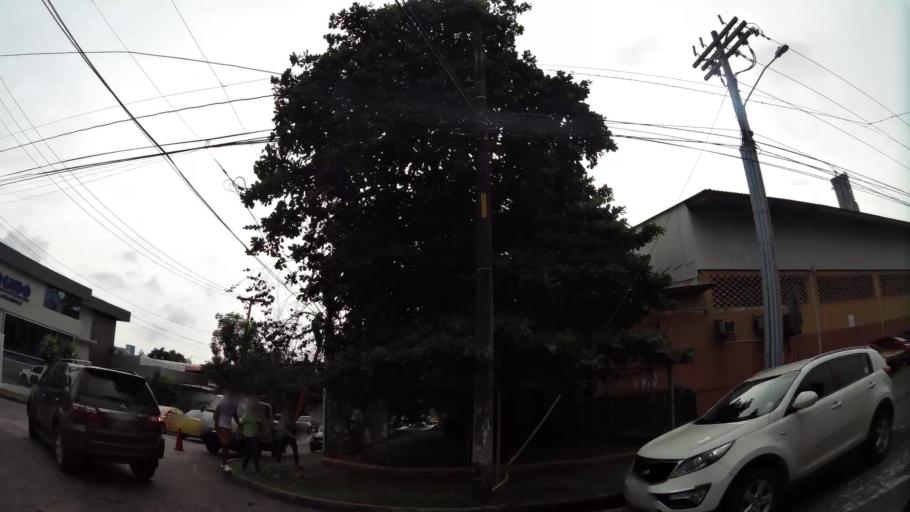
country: PA
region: Panama
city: Panama
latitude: 9.0071
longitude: -79.5311
